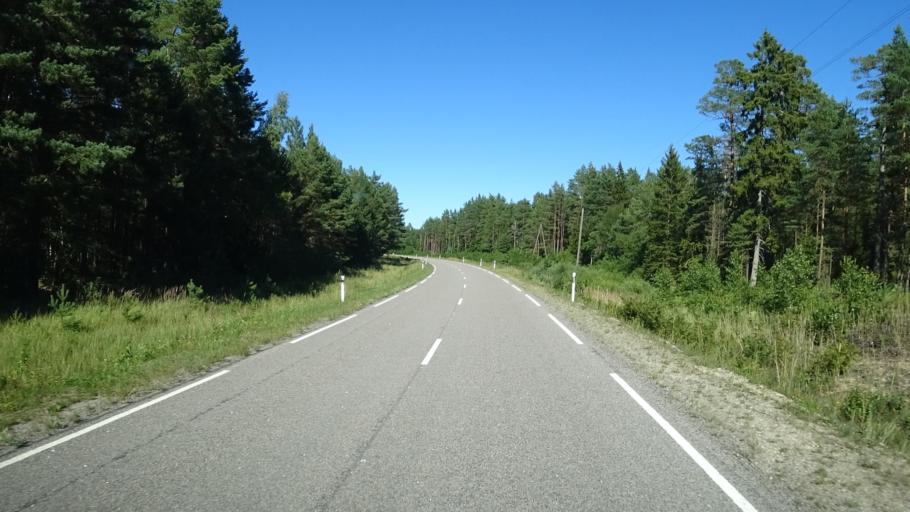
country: LV
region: Dundaga
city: Dundaga
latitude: 57.6827
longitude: 22.3634
